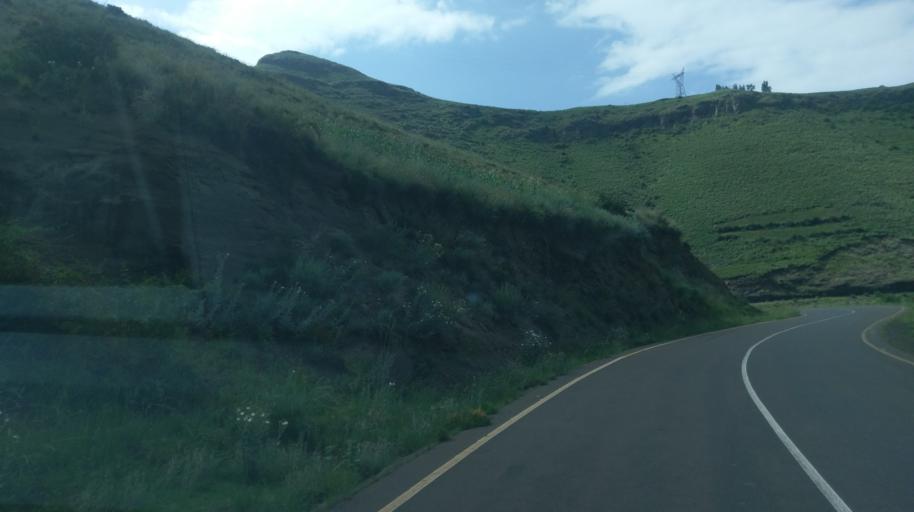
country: LS
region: Thaba-Tseka
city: Thaba-Tseka
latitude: -29.1541
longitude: 28.4799
